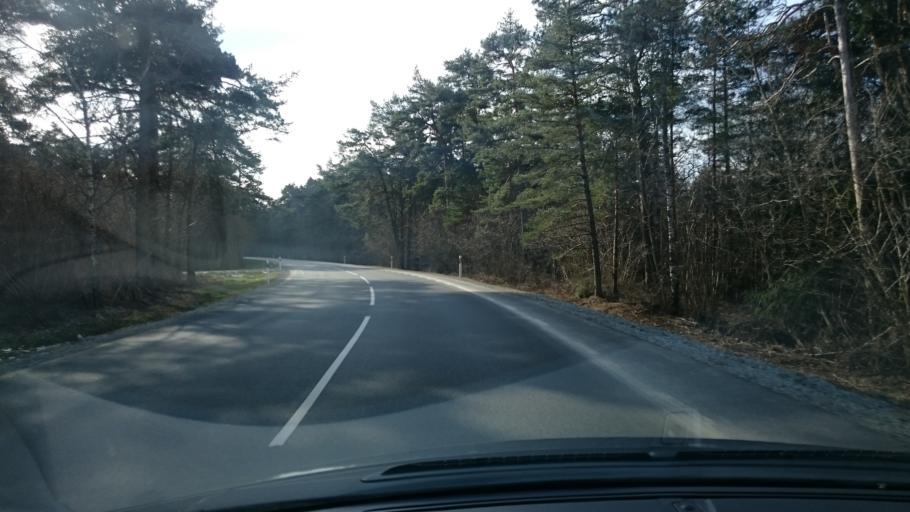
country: EE
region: Harju
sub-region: Keila linn
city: Keila
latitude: 59.3949
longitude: 24.2427
